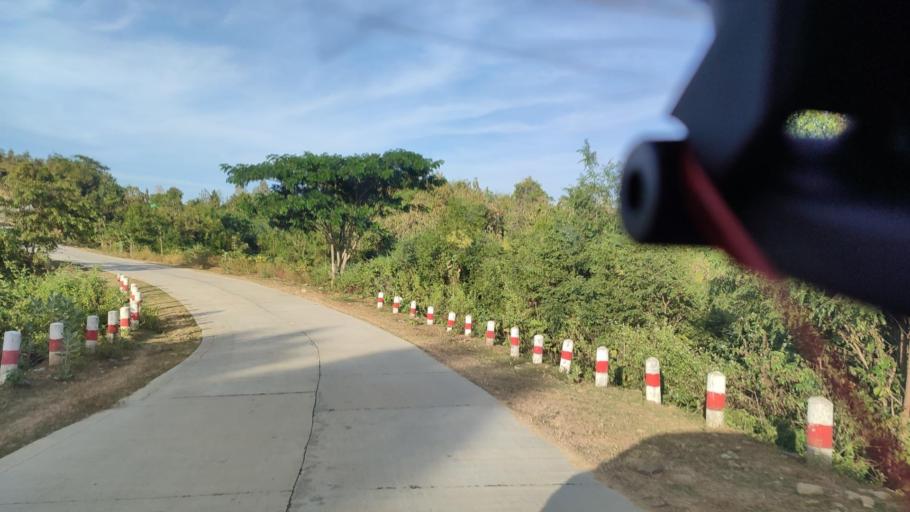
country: MM
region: Magway
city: Taungdwingyi
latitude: 20.0210
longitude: 95.8189
